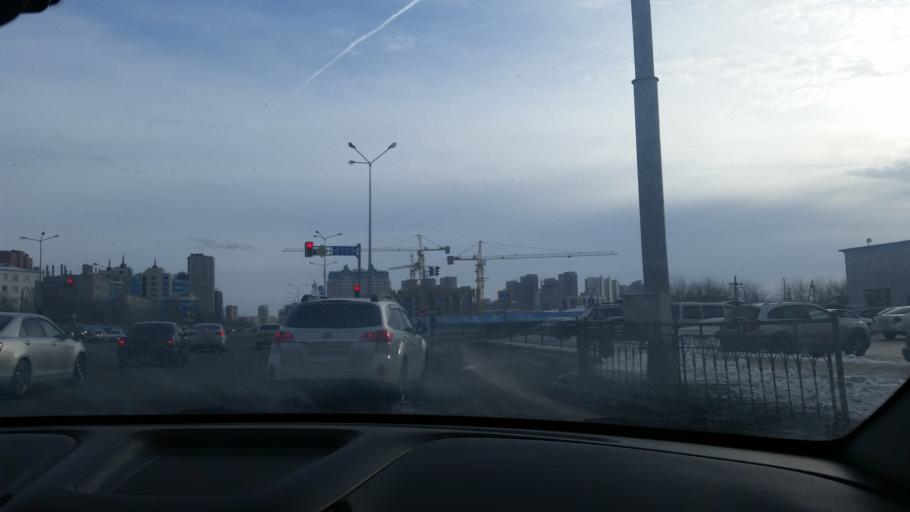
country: KZ
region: Astana Qalasy
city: Astana
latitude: 51.1459
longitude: 71.4600
